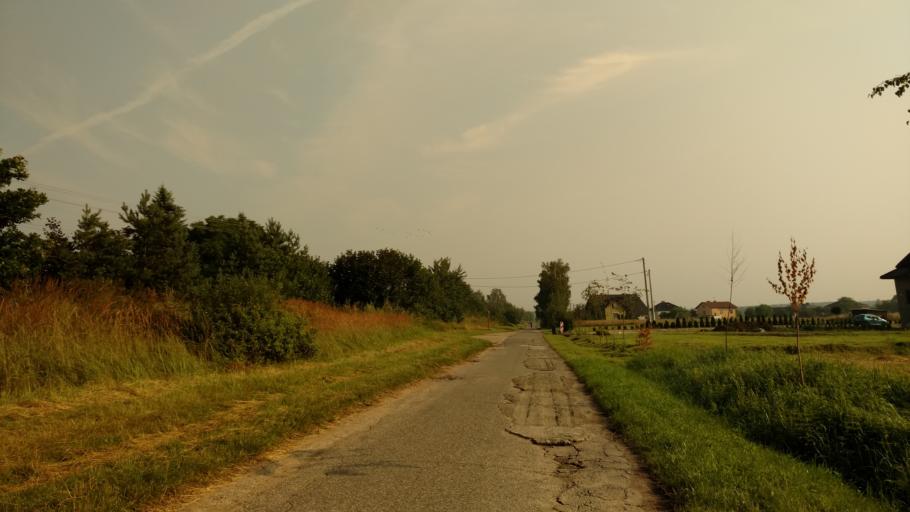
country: PL
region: Silesian Voivodeship
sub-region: Powiat pszczynski
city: Jankowice
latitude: 50.0137
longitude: 18.9744
